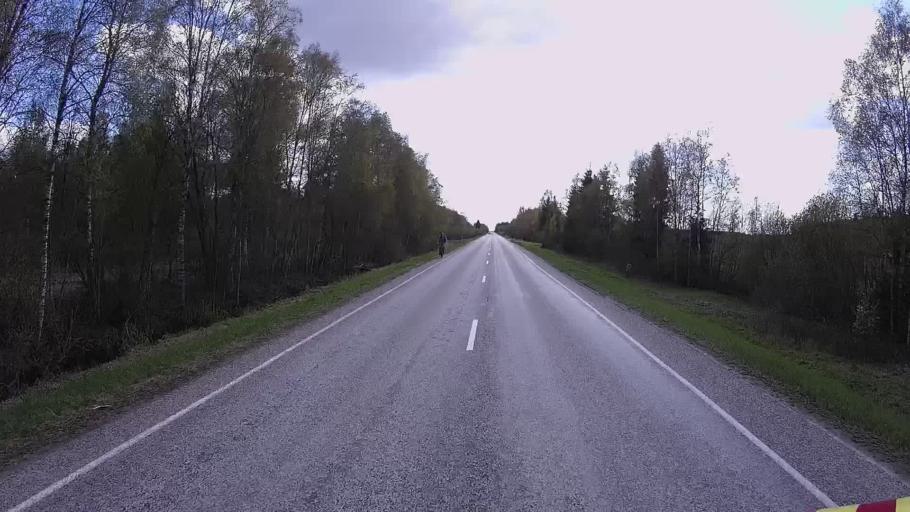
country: EE
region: Jogevamaa
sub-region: Jogeva linn
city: Jogeva
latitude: 58.7725
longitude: 26.4623
